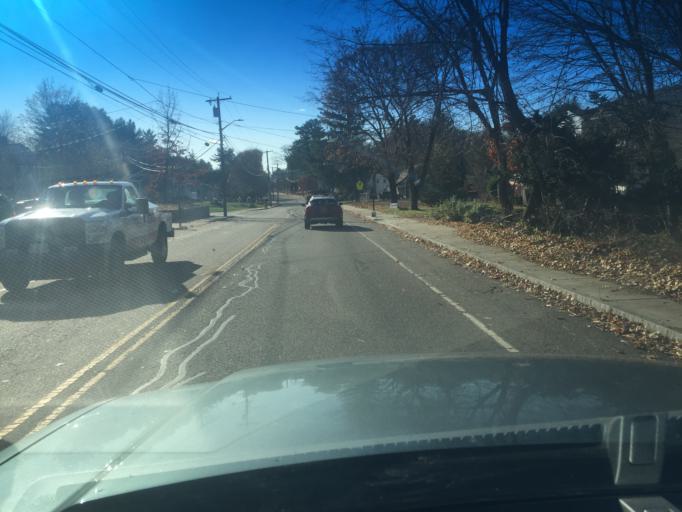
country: US
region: Massachusetts
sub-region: Norfolk County
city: Medway
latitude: 42.1154
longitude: -71.4300
